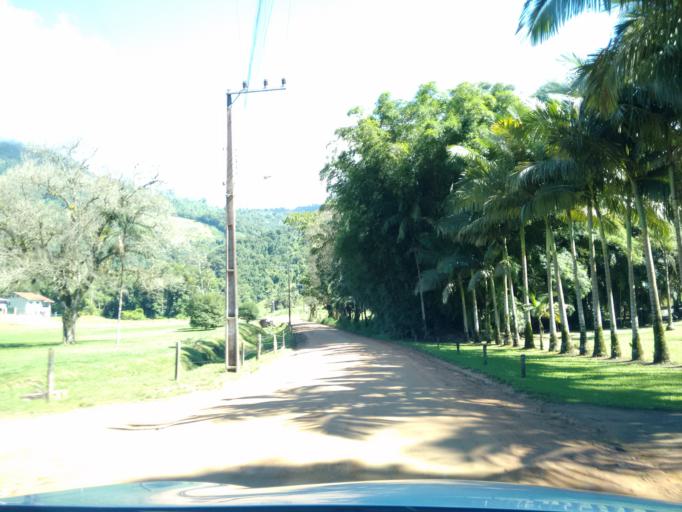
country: BR
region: Santa Catarina
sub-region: Pomerode
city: Pomerode
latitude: -26.7630
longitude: -49.1832
